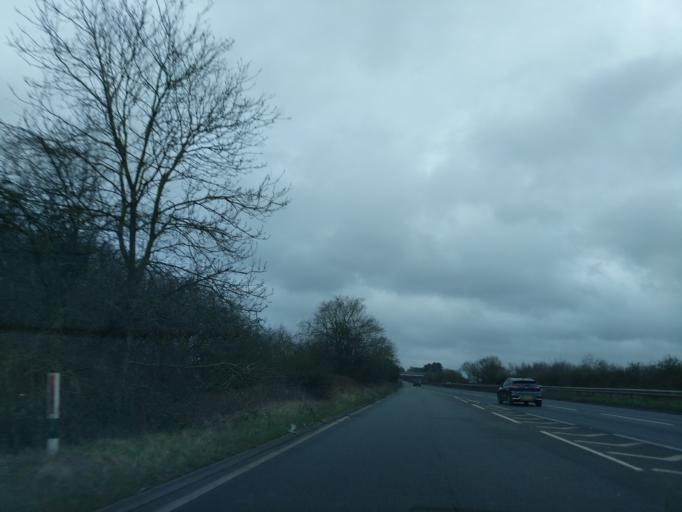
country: GB
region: England
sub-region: Staffordshire
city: Lichfield
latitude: 52.6598
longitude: -1.8171
